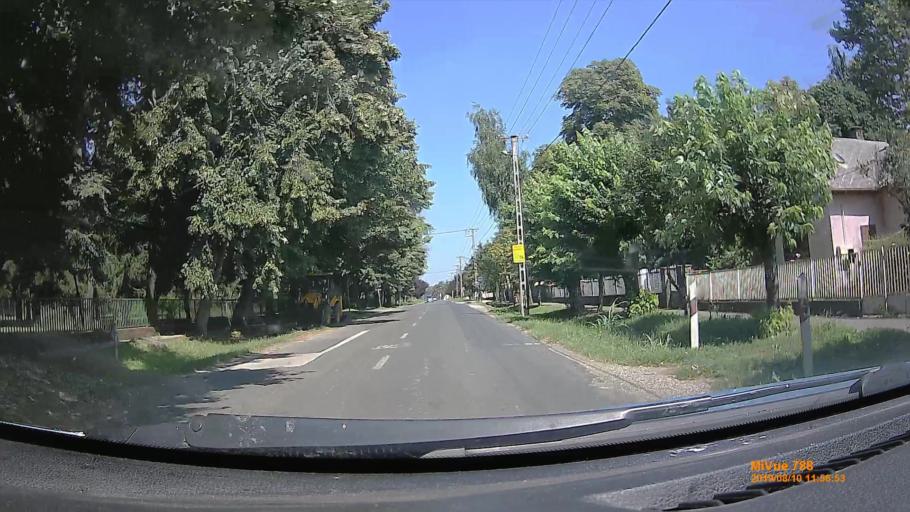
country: HU
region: Somogy
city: Somogyvar
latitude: 46.5218
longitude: 17.6690
